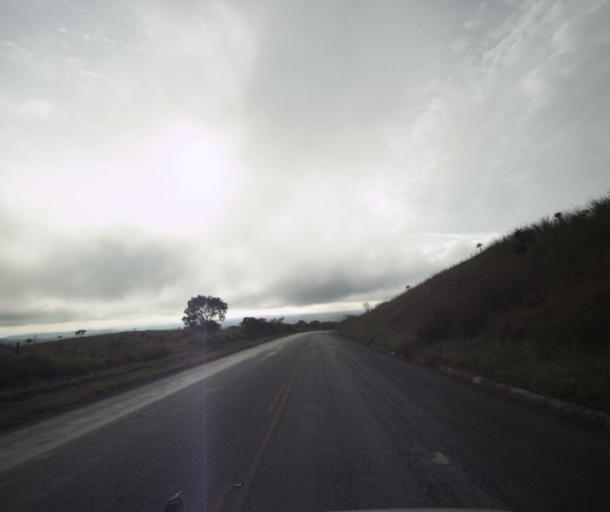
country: BR
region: Goias
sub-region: Pirenopolis
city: Pirenopolis
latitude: -15.7526
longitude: -48.7442
